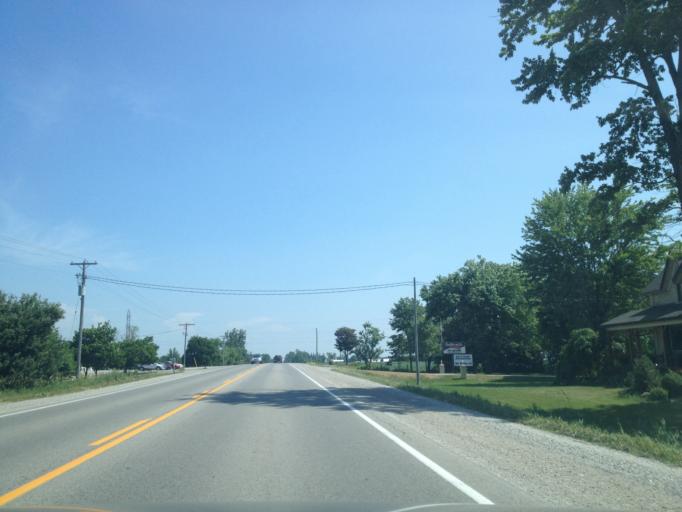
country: CA
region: Ontario
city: Huron East
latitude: 43.4407
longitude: -81.2211
